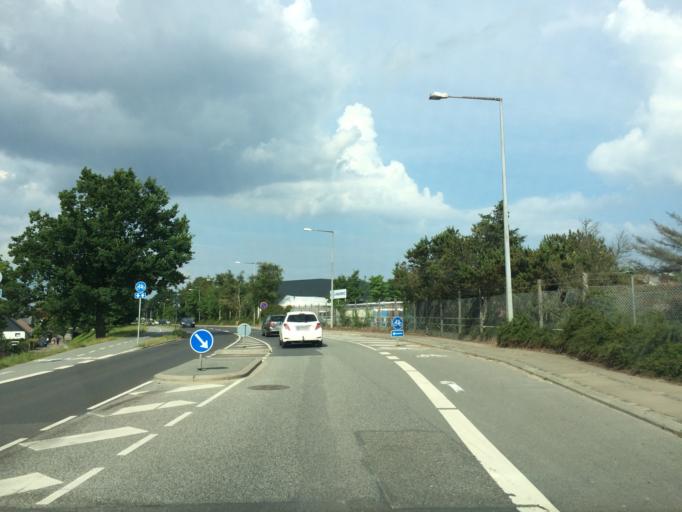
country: DK
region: South Denmark
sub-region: Middelfart Kommune
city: Middelfart
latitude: 55.5084
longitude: 9.7533
